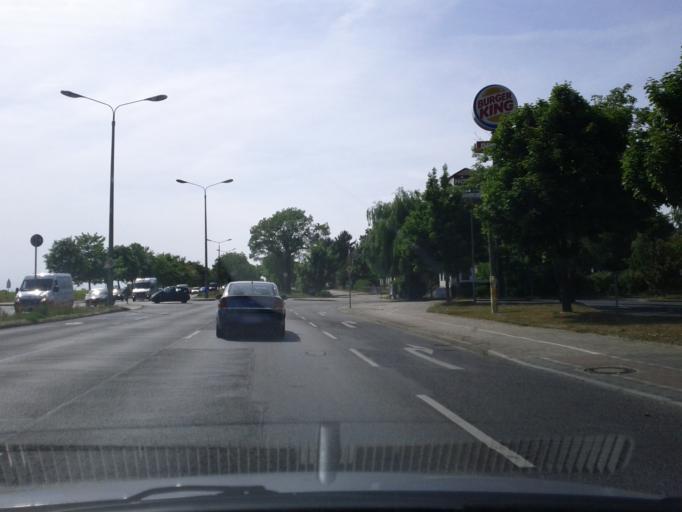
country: DE
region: Berlin
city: Mahlsdorf
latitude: 52.5050
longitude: 13.6073
